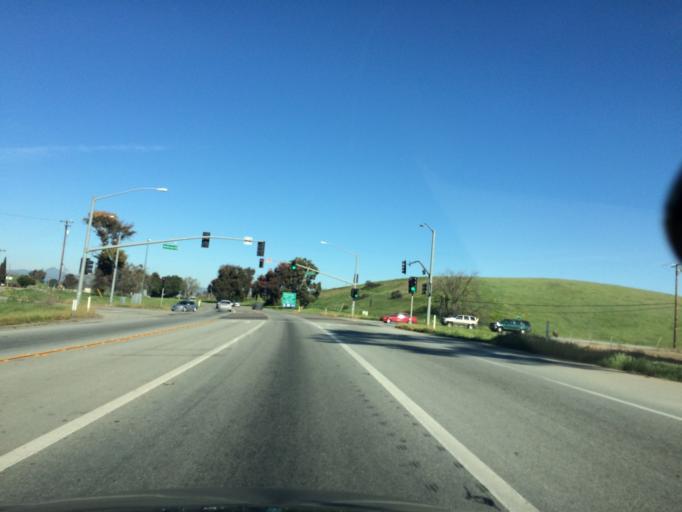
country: US
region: California
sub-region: San Benito County
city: Hollister
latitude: 36.8421
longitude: -121.4584
